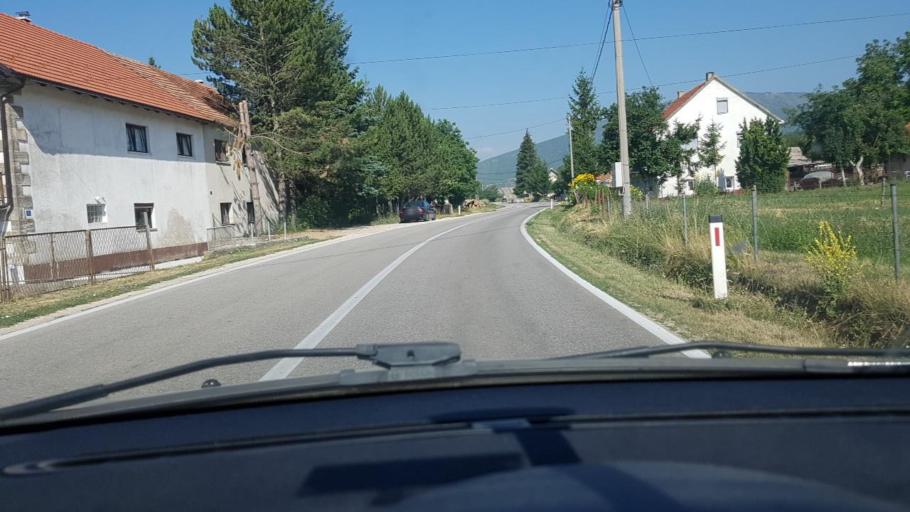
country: BA
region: Federation of Bosnia and Herzegovina
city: Zabrisce
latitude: 43.8540
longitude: 16.9459
